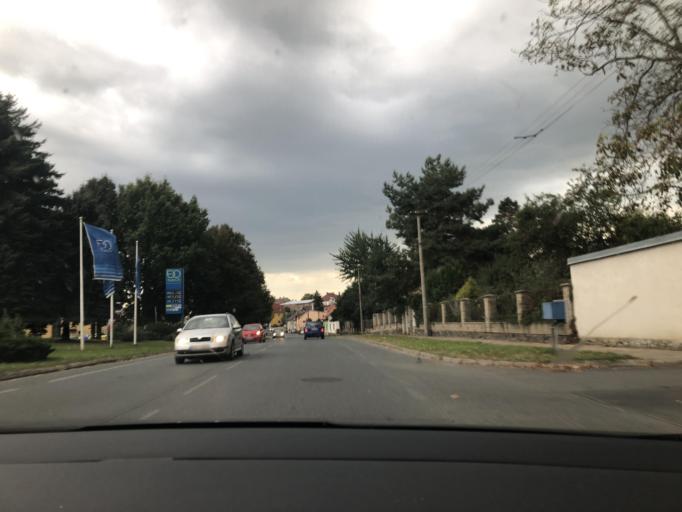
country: CZ
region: Central Bohemia
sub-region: Okres Kolin
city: Tynec nad Labem
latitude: 50.0465
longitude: 15.3624
